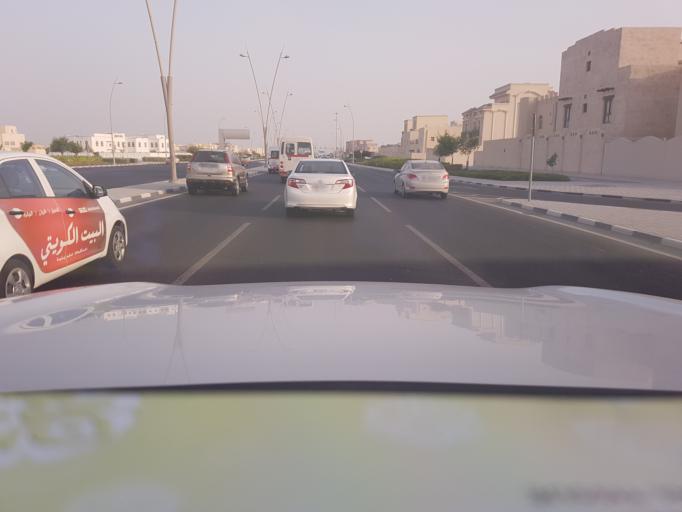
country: QA
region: Baladiyat ad Dawhah
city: Doha
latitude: 25.2369
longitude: 51.5488
